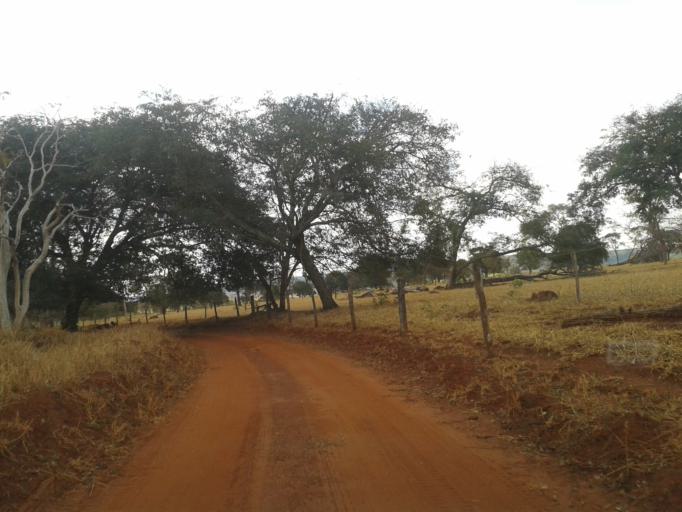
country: BR
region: Minas Gerais
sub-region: Santa Vitoria
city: Santa Vitoria
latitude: -19.1941
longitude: -49.9735
